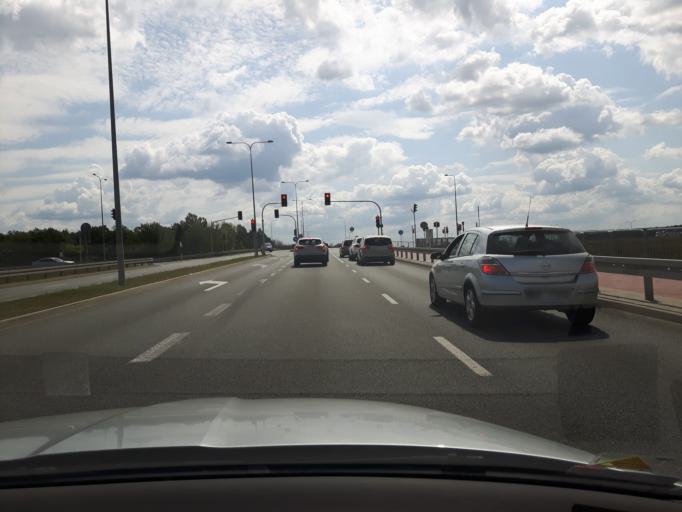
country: PL
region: Masovian Voivodeship
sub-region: Powiat pruszkowski
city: Nadarzyn
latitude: 52.1079
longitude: 20.8357
